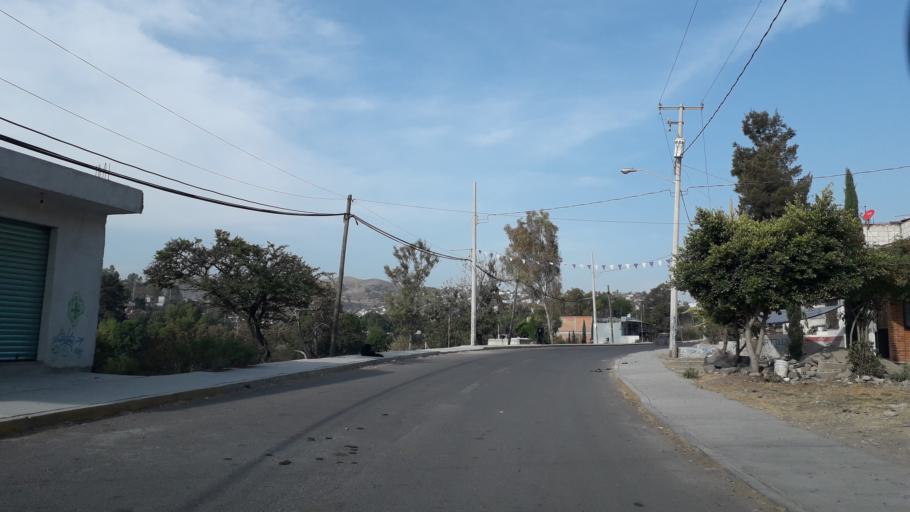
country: MX
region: Puebla
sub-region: Puebla
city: San Andres Azumiatla
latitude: 18.9043
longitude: -98.2478
